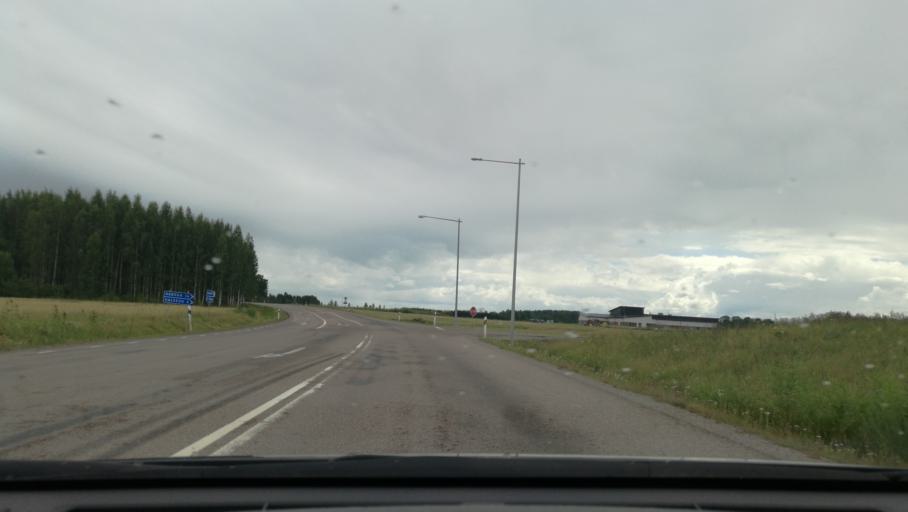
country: SE
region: Vaestmanland
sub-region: Kopings Kommun
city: Koping
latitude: 59.4845
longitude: 15.9845
